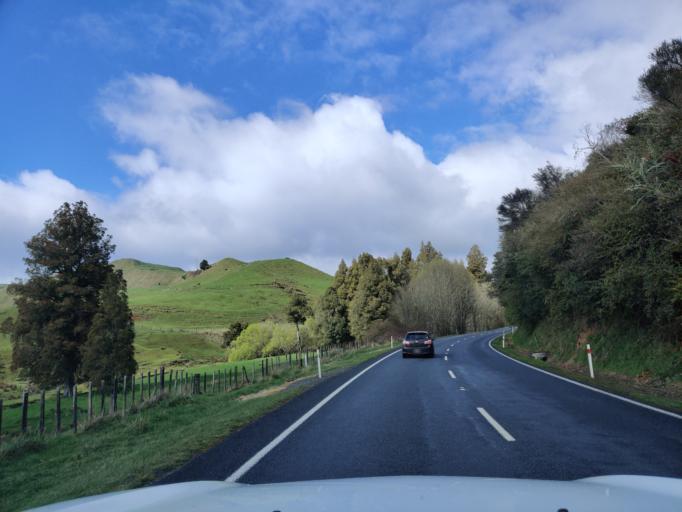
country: NZ
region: Waikato
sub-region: Otorohanga District
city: Otorohanga
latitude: -38.5938
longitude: 175.2196
